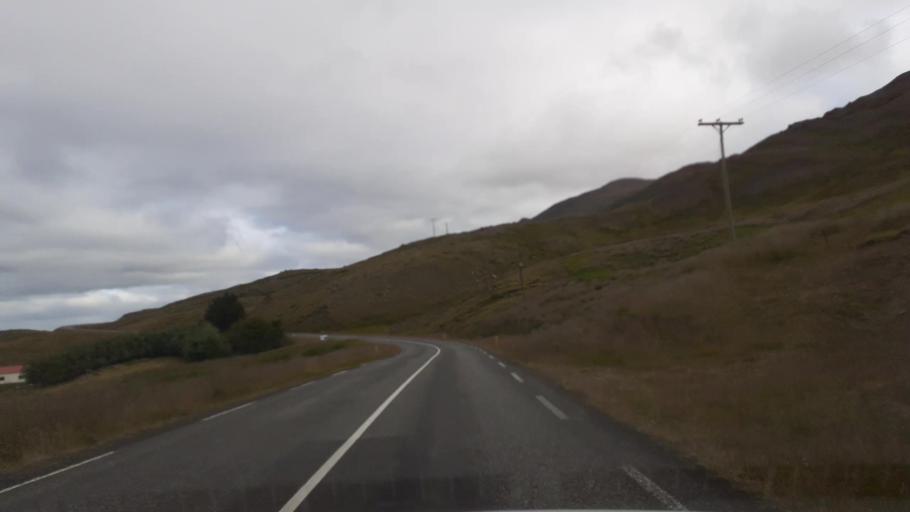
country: IS
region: Northeast
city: Akureyri
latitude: 65.8207
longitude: -18.0502
